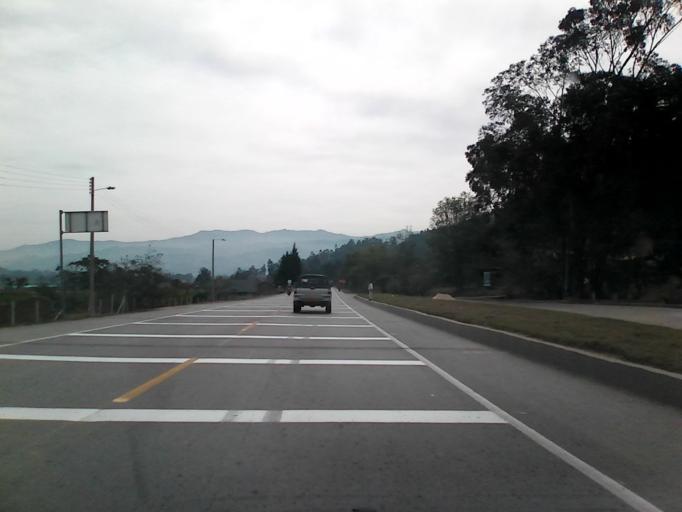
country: CO
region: Boyaca
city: Tibasosa
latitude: 5.7457
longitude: -72.9915
